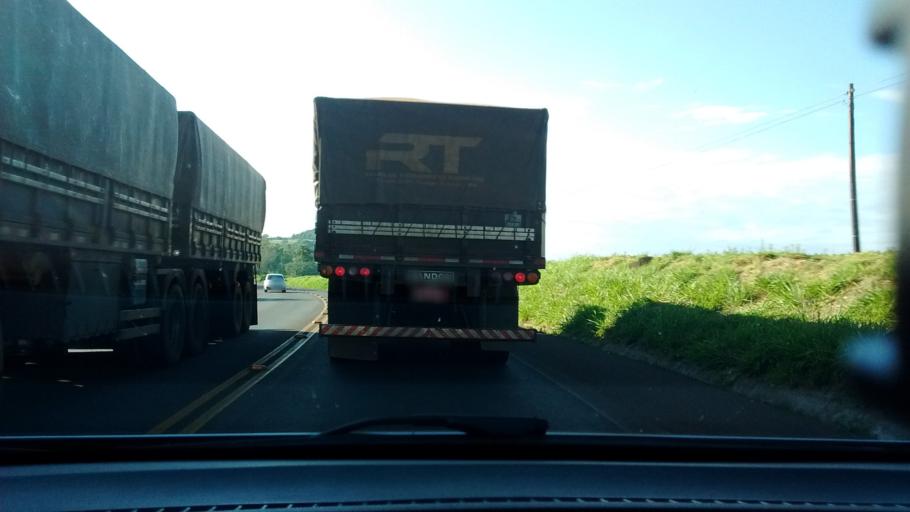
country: BR
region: Parana
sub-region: Cascavel
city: Cascavel
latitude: -25.2268
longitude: -53.5916
